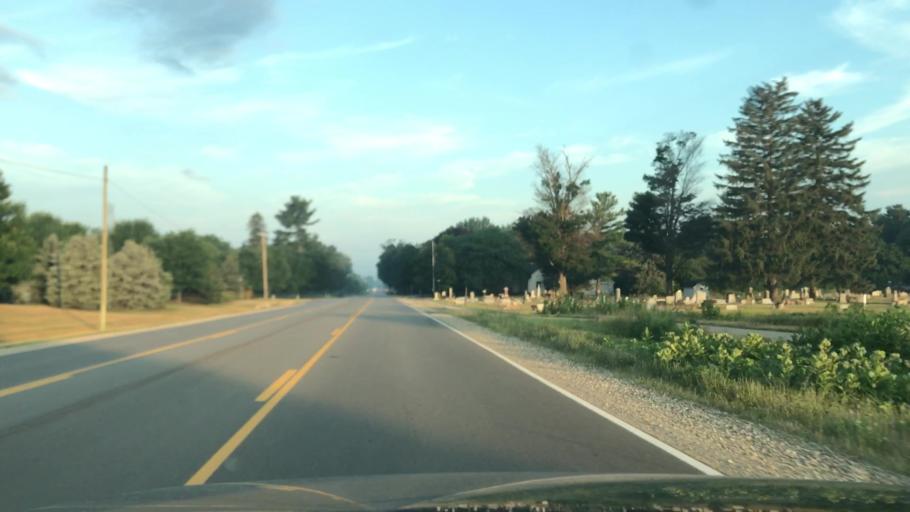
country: US
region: Michigan
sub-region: Ottawa County
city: Zeeland
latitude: 42.7833
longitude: -85.9737
